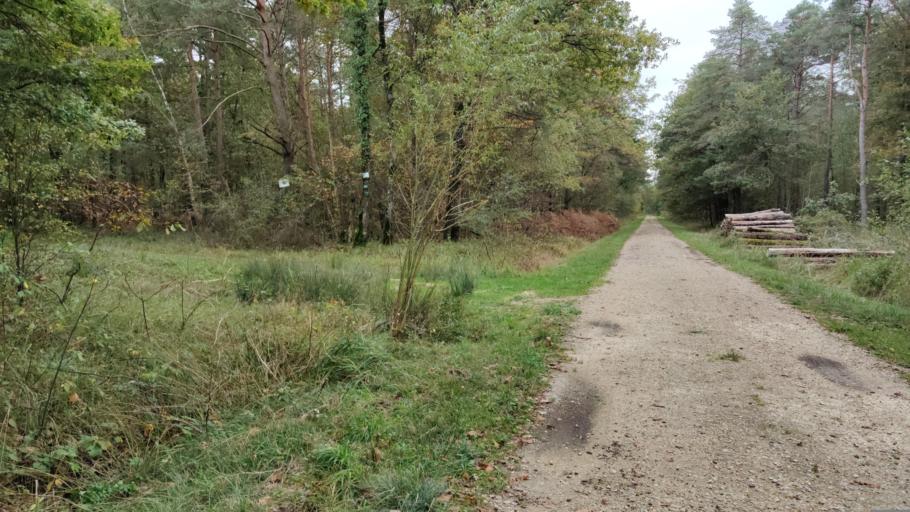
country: FR
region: Centre
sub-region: Departement du Loiret
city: Chanteau
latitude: 47.9660
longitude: 1.9367
